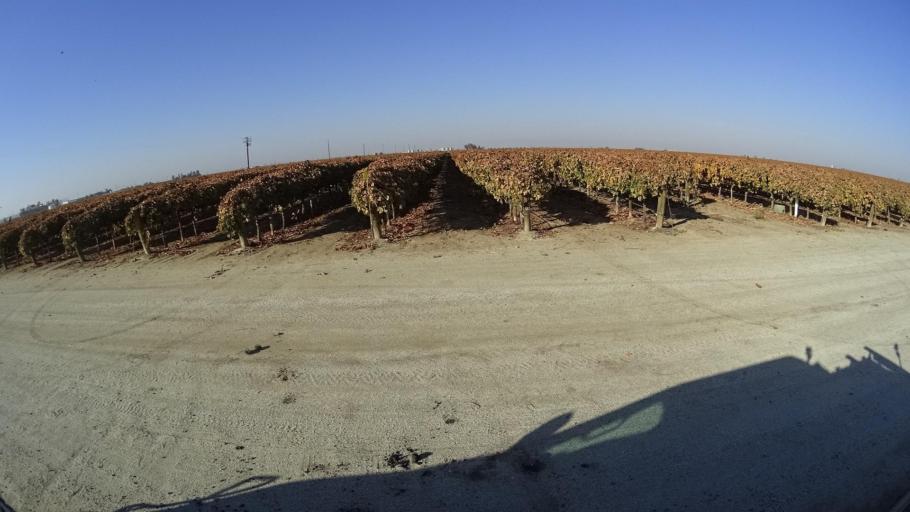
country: US
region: California
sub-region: Tulare County
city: Richgrove
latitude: 35.7830
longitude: -119.1698
